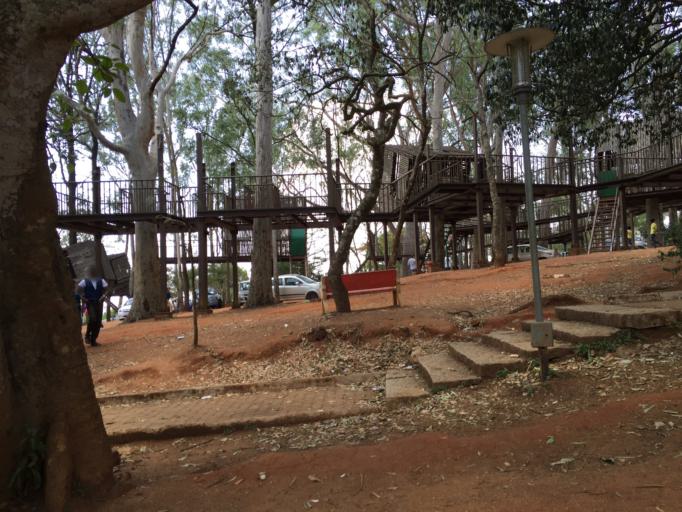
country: IN
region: Karnataka
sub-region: Chikkaballapur
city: Chik Ballapur
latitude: 13.3692
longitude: 77.6830
